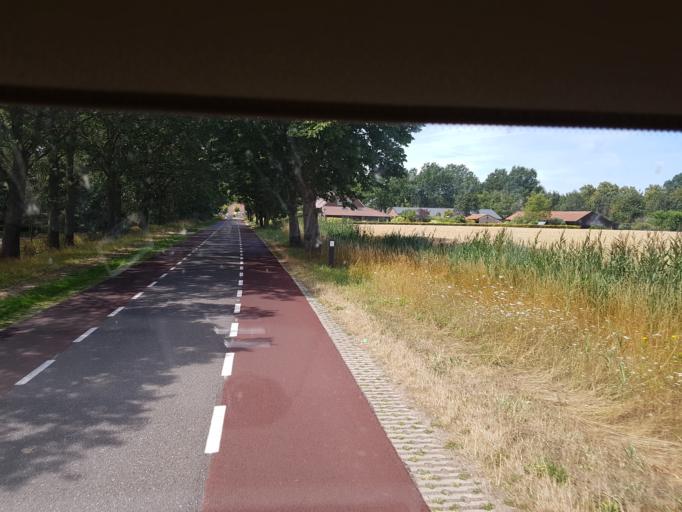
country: NL
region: Limburg
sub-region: Gemeente Leudal
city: Kelpen-Oler
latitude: 51.2237
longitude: 5.8022
